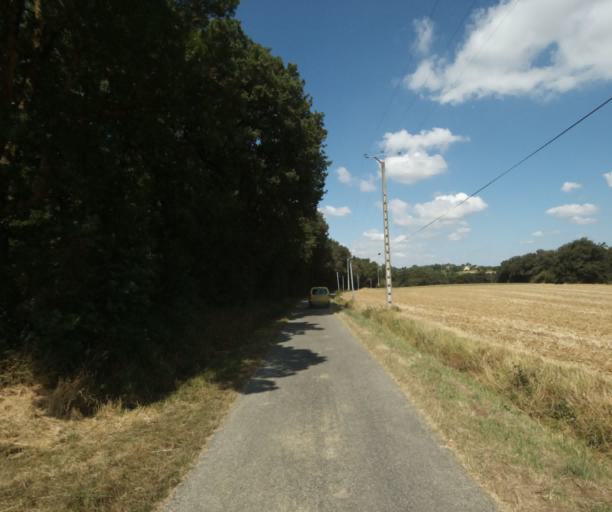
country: FR
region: Midi-Pyrenees
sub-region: Departement de la Haute-Garonne
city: Auriac-sur-Vendinelle
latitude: 43.4592
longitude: 1.8042
